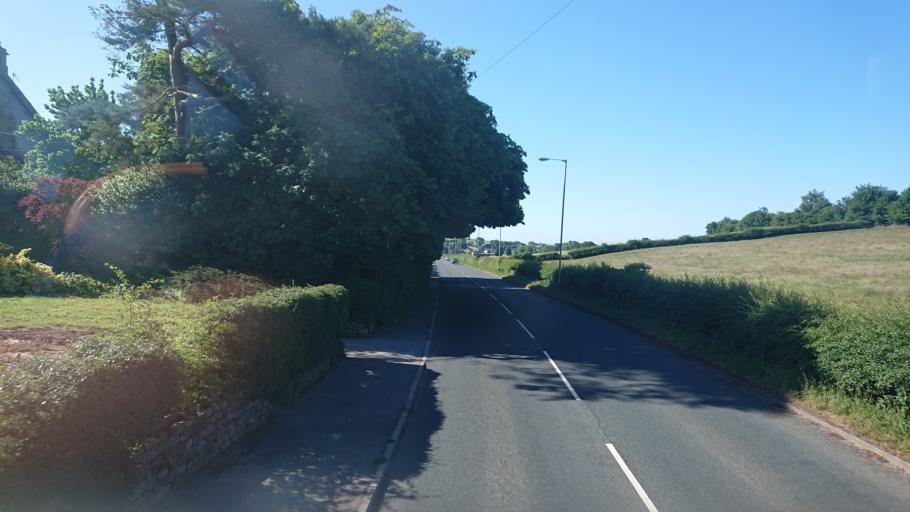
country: GB
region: England
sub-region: Lancashire
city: Galgate
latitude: 54.0004
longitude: -2.7920
